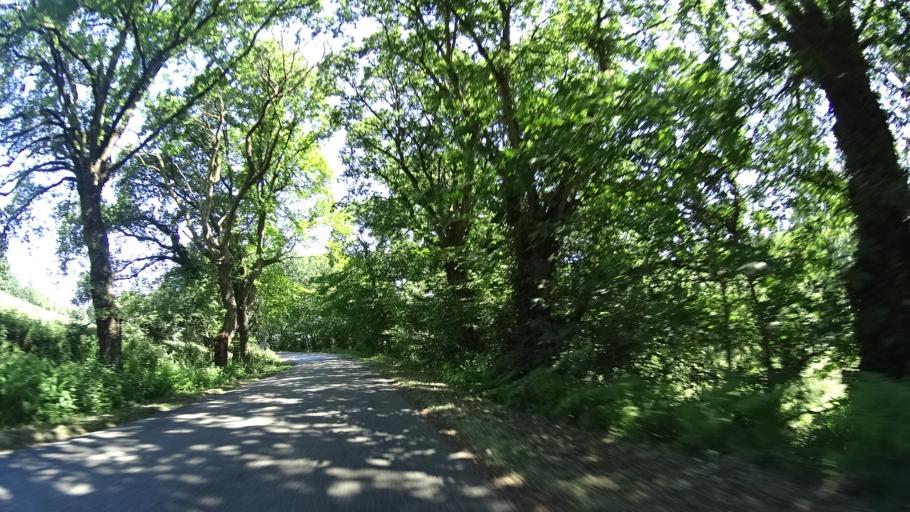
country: FR
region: Brittany
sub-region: Departement d'Ille-et-Vilaine
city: Langon
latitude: 47.7704
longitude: -1.8460
